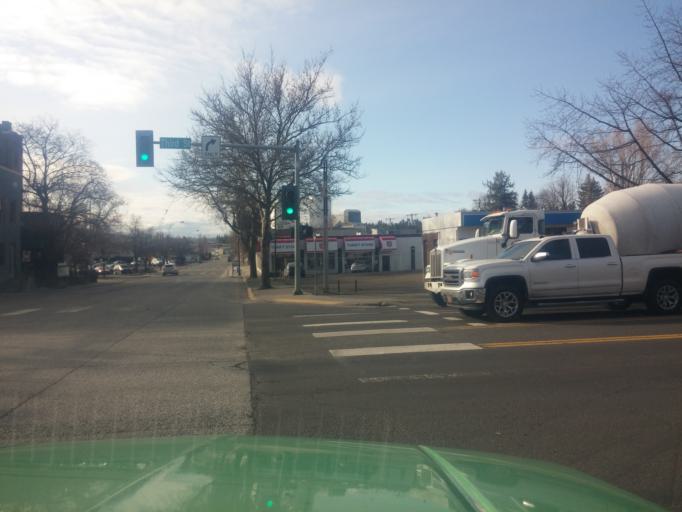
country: US
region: Idaho
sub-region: Latah County
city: Moscow
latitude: 46.7325
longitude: -117.0028
